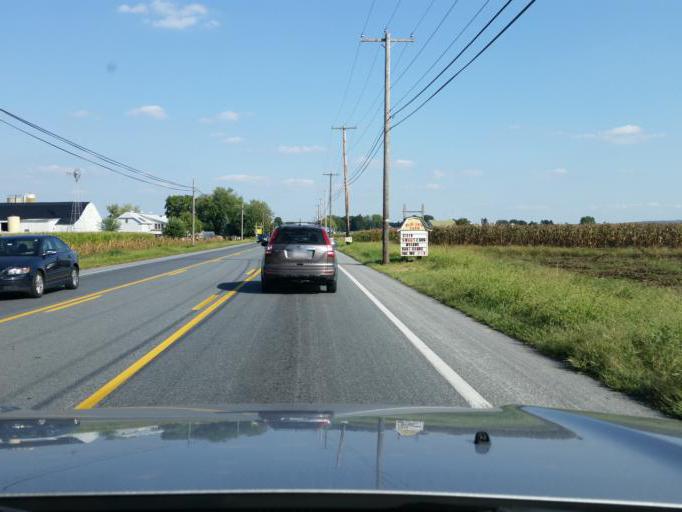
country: US
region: Pennsylvania
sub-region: Lancaster County
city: Strasburg
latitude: 40.0186
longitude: -76.1734
